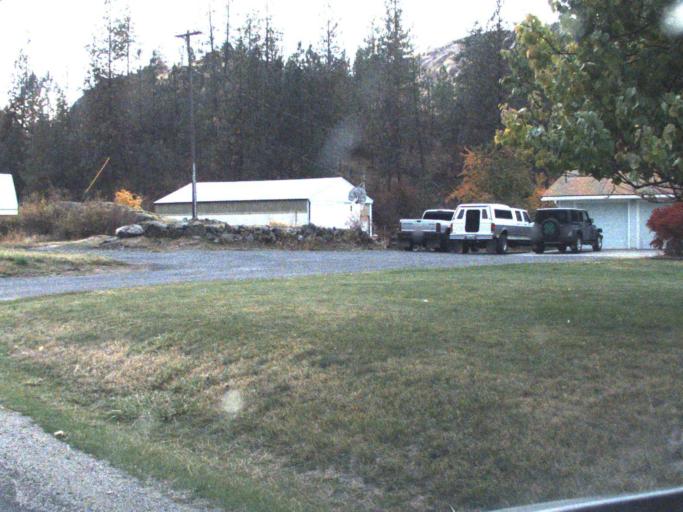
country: US
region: Washington
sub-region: Lincoln County
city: Davenport
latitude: 48.1128
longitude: -118.2020
